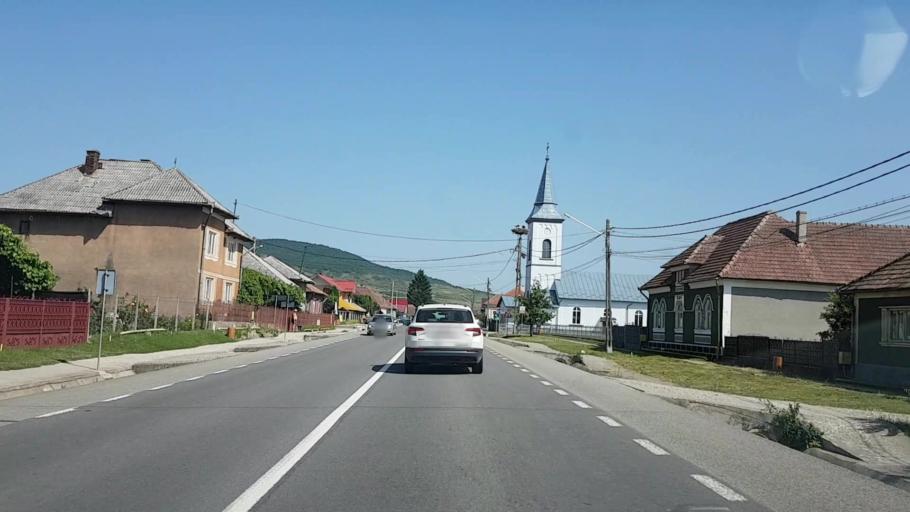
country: RO
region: Bistrita-Nasaud
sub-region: Comuna Sieu-Magherus
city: Sieu-Magherus
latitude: 47.0899
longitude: 24.3753
